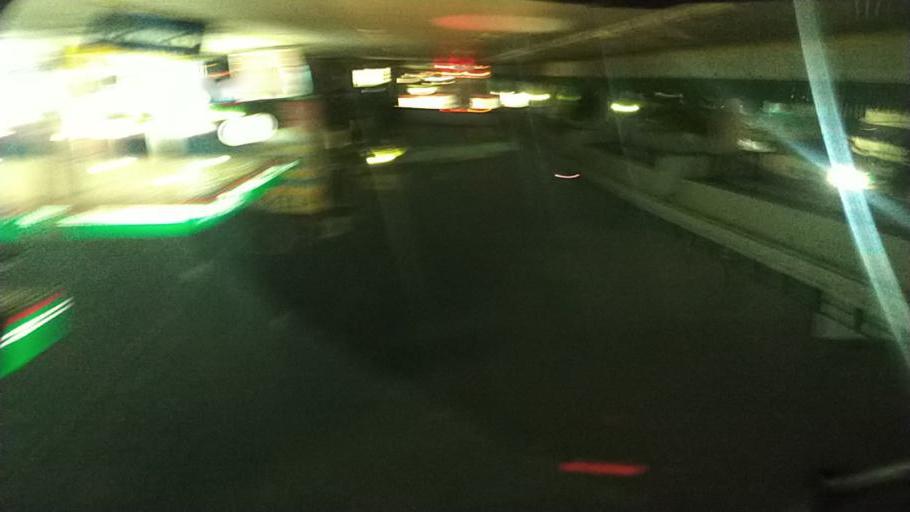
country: MX
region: Mexico
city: Ecatepec
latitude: 19.6259
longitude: -99.0786
